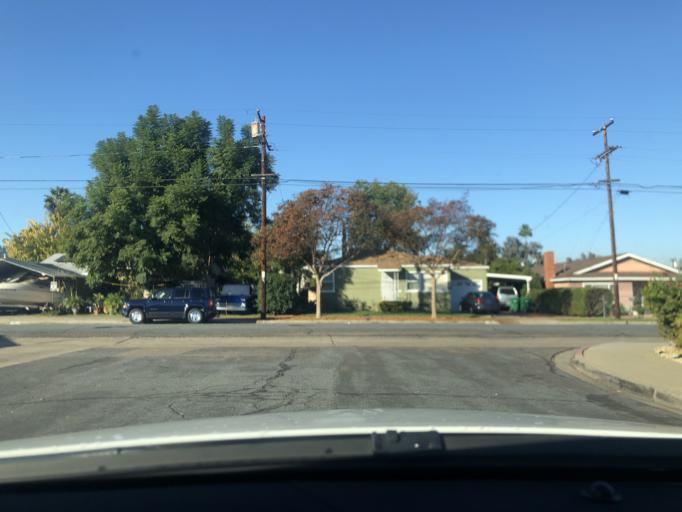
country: US
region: California
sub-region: San Diego County
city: El Cajon
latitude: 32.7820
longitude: -116.9597
